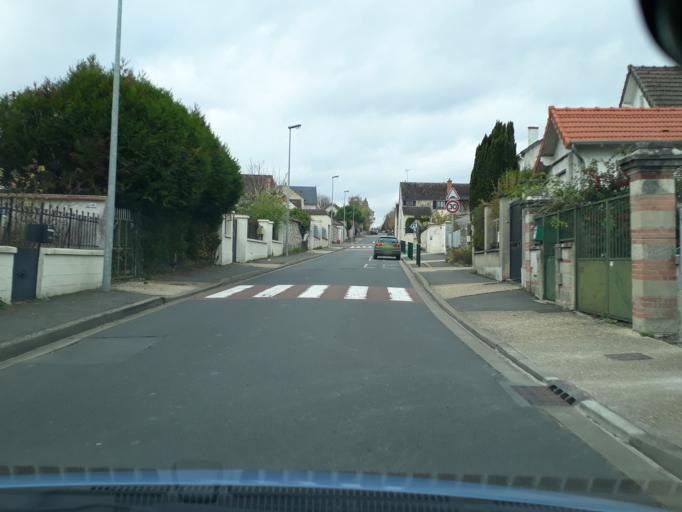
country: FR
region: Ile-de-France
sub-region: Departement de Seine-et-Marne
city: Veneux-les-Sablons
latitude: 48.3824
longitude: 2.7858
